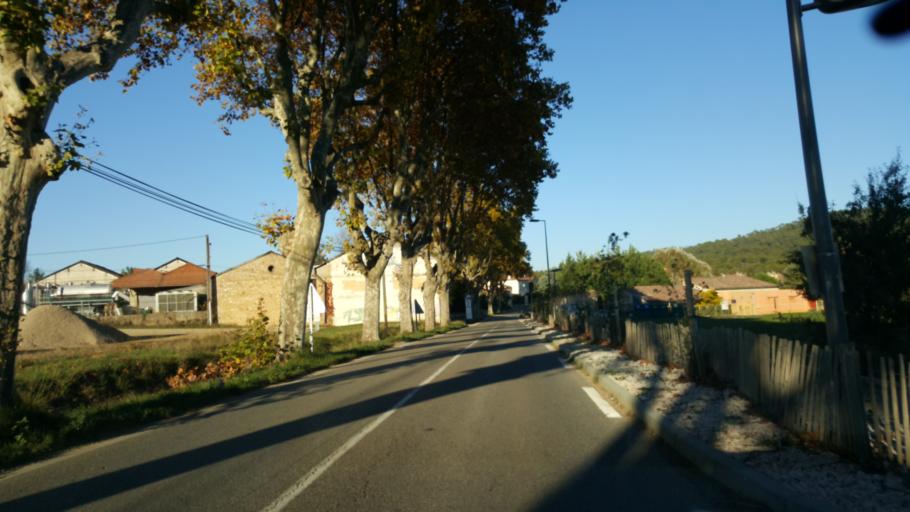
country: FR
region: Provence-Alpes-Cote d'Azur
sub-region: Departement du Var
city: Bras
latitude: 43.5249
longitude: 5.9407
